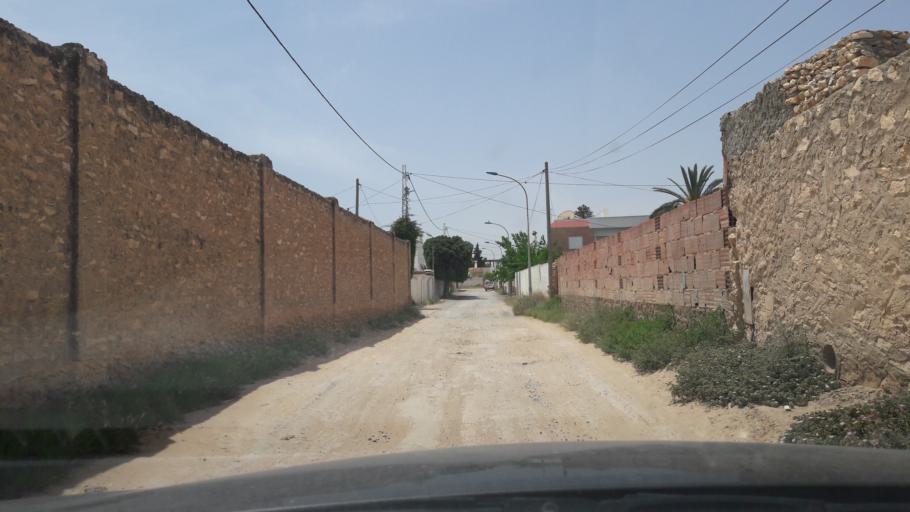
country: TN
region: Safaqis
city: Al Qarmadah
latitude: 34.7831
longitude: 10.7587
